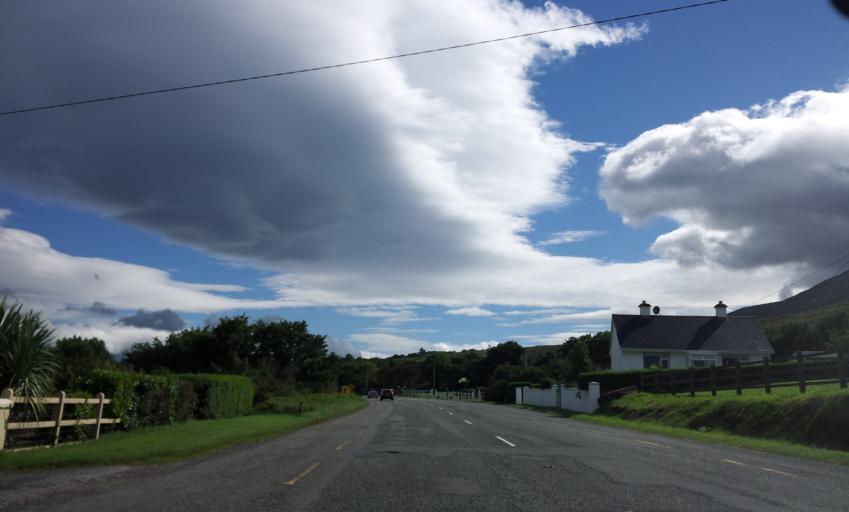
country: IE
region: Munster
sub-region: Ciarrai
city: Killorglin
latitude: 52.2337
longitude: -9.8558
